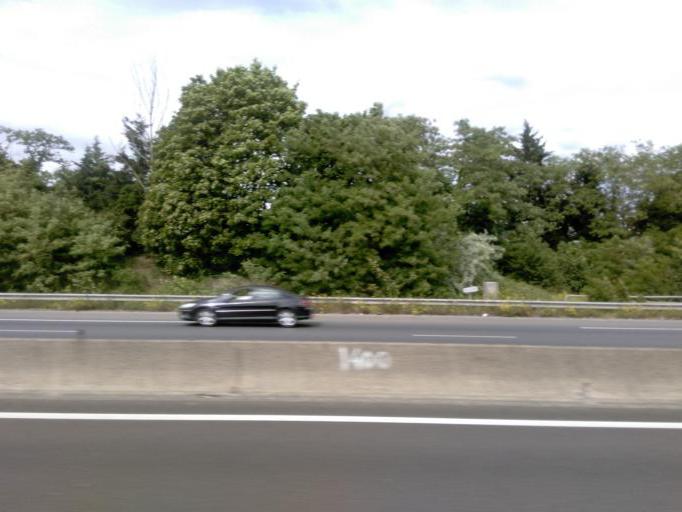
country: FR
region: Ile-de-France
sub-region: Departement du Val-d'Oise
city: Herblay
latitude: 49.0044
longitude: 2.1670
